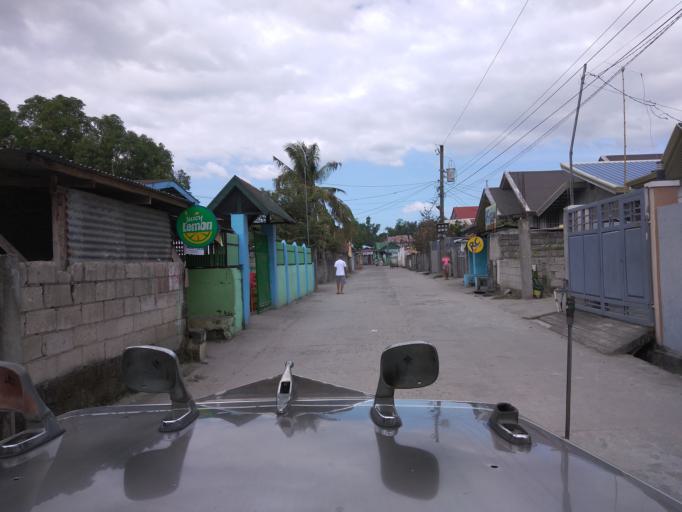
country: PH
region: Central Luzon
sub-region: Province of Pampanga
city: San Patricio
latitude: 15.1158
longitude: 120.7088
